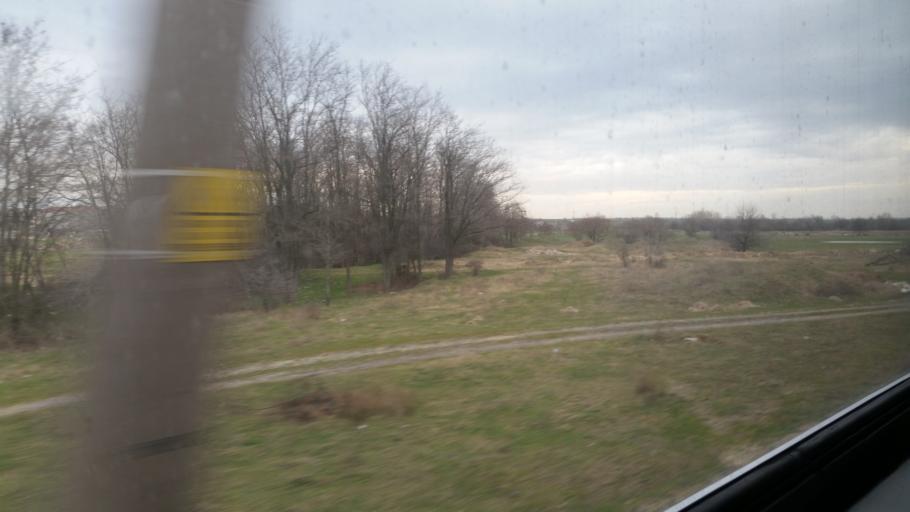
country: TR
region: Tekirdag
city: Velimese
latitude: 41.2506
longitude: 27.8902
